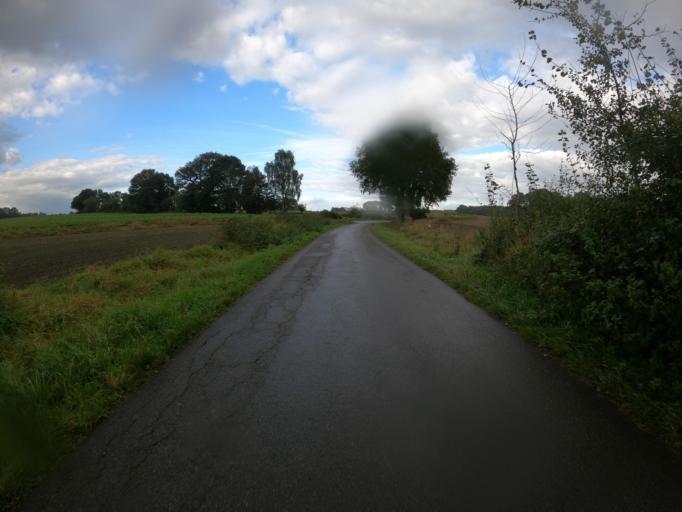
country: DE
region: North Rhine-Westphalia
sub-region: Regierungsbezirk Dusseldorf
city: Schermbeck
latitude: 51.7272
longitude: 6.8729
